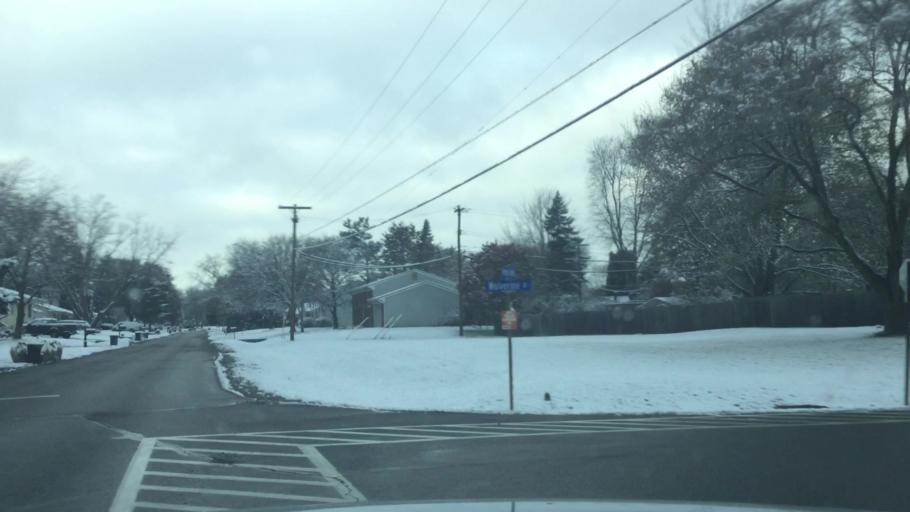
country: US
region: Michigan
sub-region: Oakland County
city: Walled Lake
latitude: 42.5445
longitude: -83.4824
